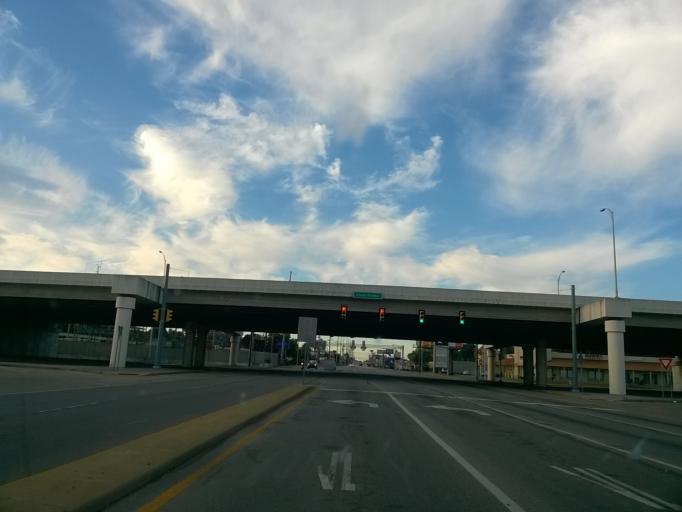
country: US
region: Indiana
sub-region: Vanderburgh County
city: Melody Hill
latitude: 37.9771
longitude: -87.4926
